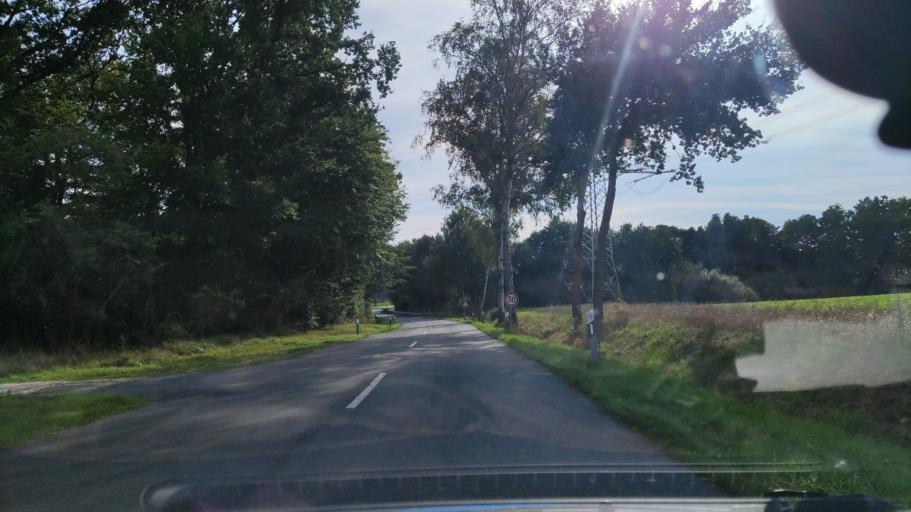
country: DE
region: Lower Saxony
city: Gerdau
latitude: 52.9902
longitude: 10.3810
